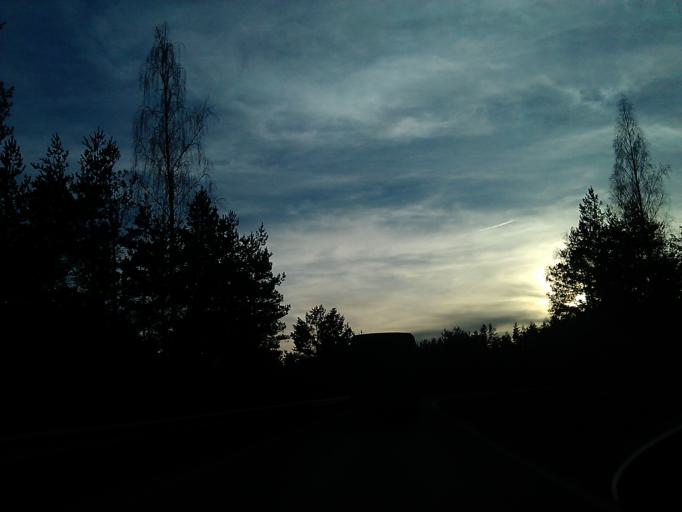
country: LV
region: Riga
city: Bergi
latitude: 57.0093
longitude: 24.3102
